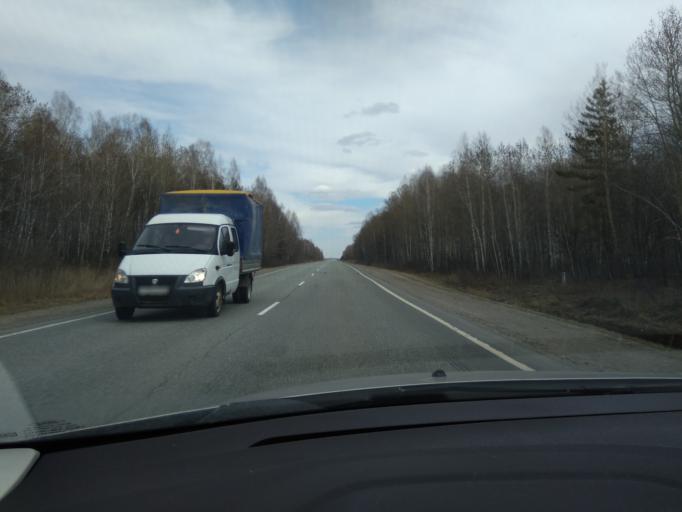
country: RU
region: Sverdlovsk
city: Yelanskiy
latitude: 56.7653
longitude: 62.4201
